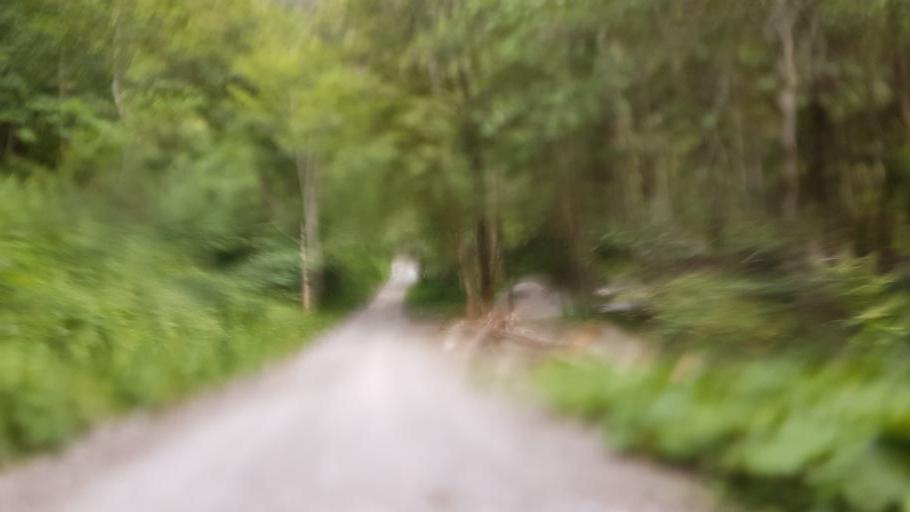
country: CH
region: Bern
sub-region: Obersimmental-Saanen District
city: Boltigen
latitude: 46.6735
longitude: 7.4565
